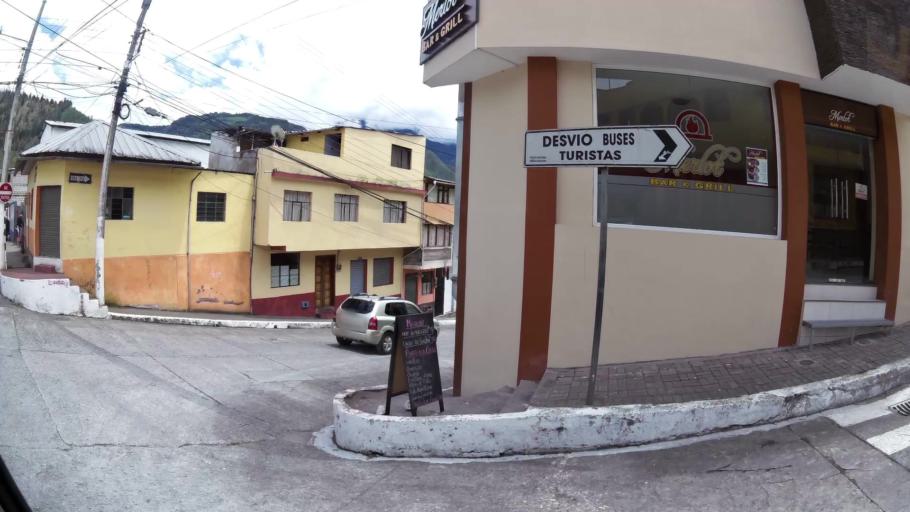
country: EC
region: Tungurahua
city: Banos
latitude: -1.3975
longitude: -78.4277
